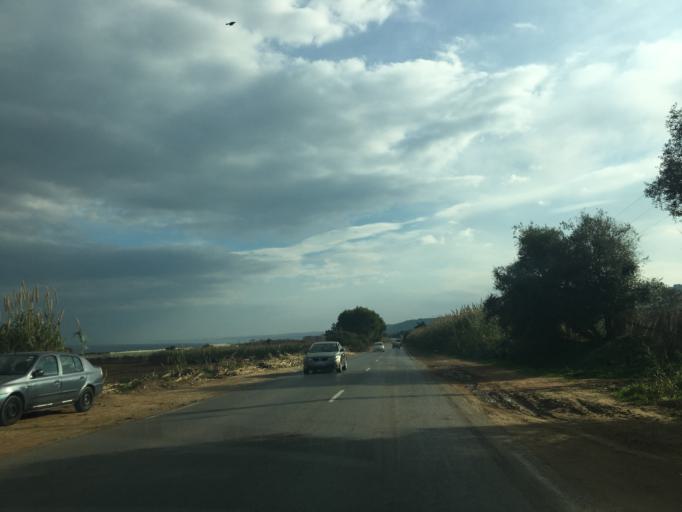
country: DZ
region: Tipaza
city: Tipasa
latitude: 36.5896
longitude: 2.5023
